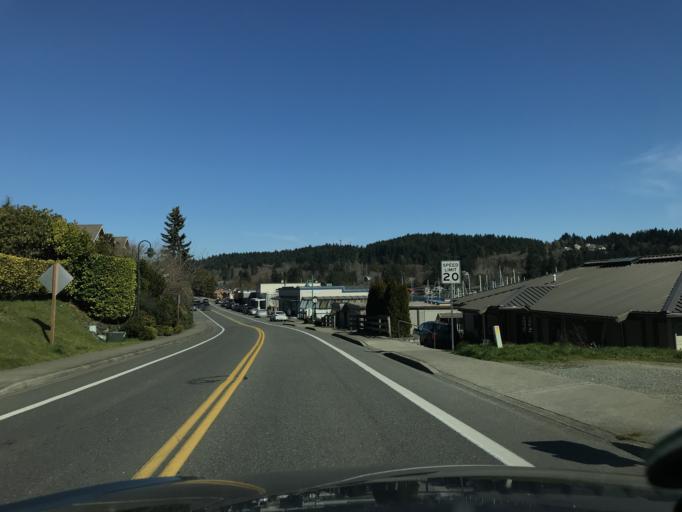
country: US
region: Washington
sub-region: Pierce County
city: Gig Harbor
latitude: 47.3380
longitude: -122.5918
